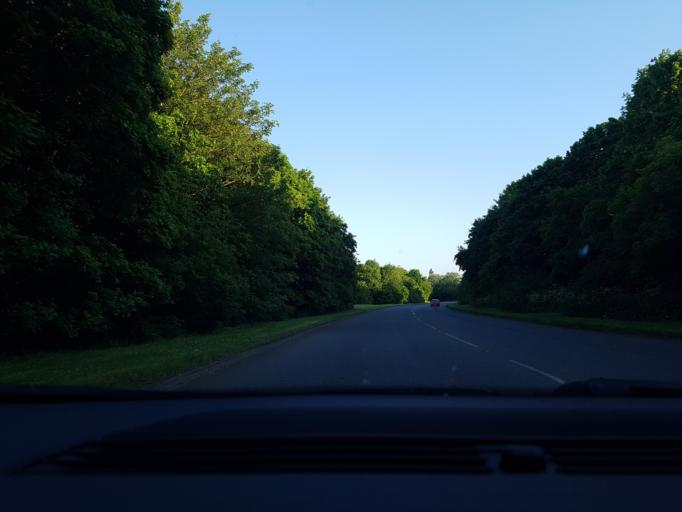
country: GB
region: England
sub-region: Buckinghamshire
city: Buckingham
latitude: 51.9991
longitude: -0.9698
